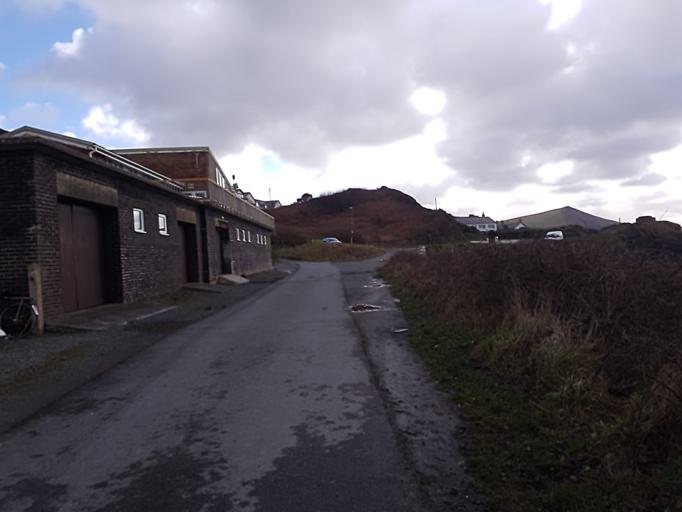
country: GB
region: Wales
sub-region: County of Ceredigion
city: Aberystwyth
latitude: 52.4074
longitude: -4.0882
